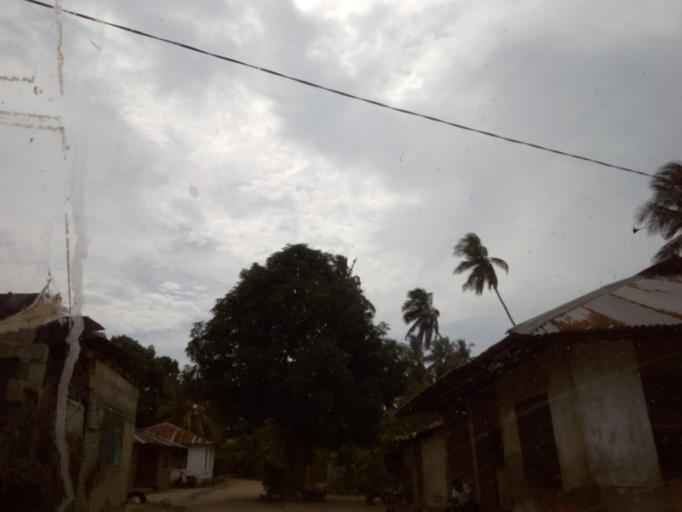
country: TZ
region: Zanzibar Central/South
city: Mahonda
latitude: -6.3324
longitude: 39.4002
